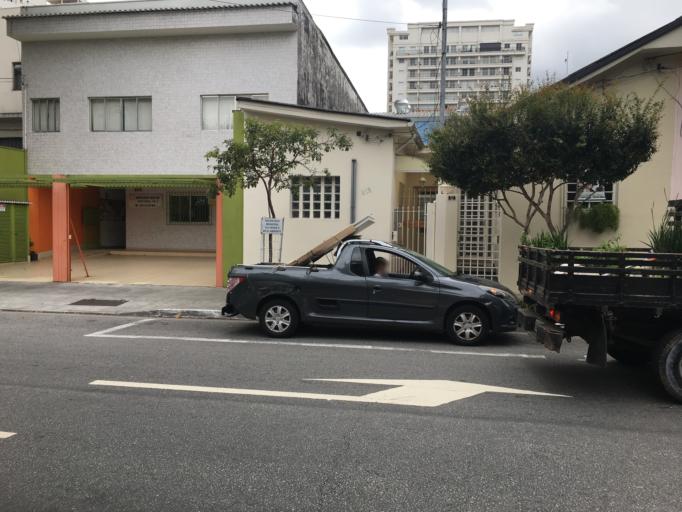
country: BR
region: Sao Paulo
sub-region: Sao Paulo
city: Sao Paulo
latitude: -23.5673
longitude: -46.6993
